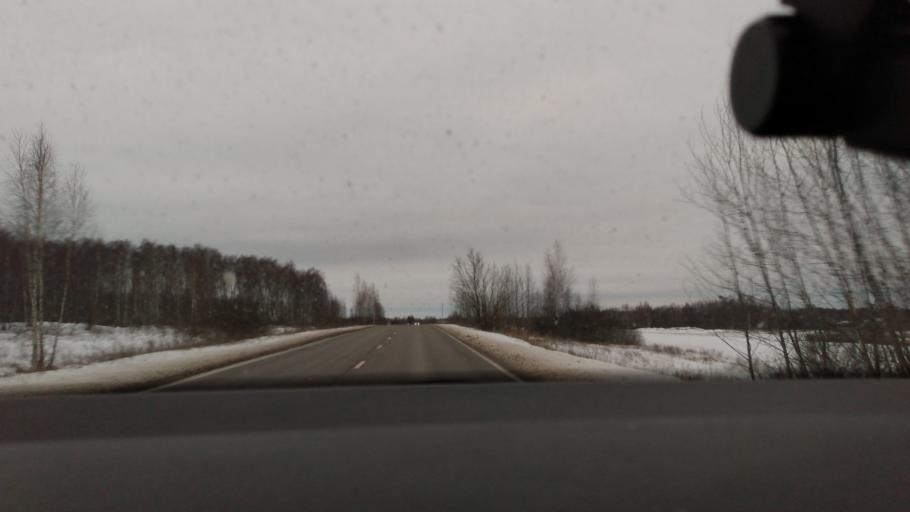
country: RU
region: Moskovskaya
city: Krasnaya Poyma
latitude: 55.1497
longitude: 39.2182
